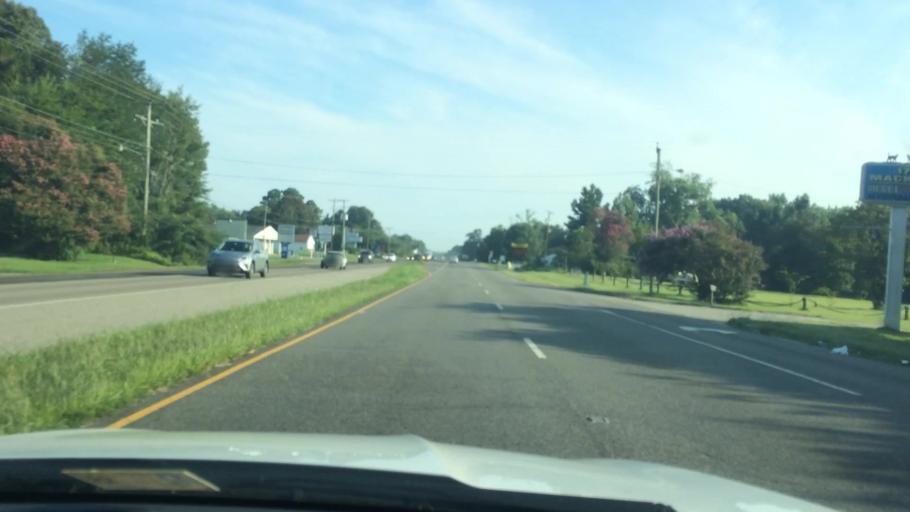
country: US
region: Virginia
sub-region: Gloucester County
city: Gloucester Point
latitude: 37.3059
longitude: -76.5128
